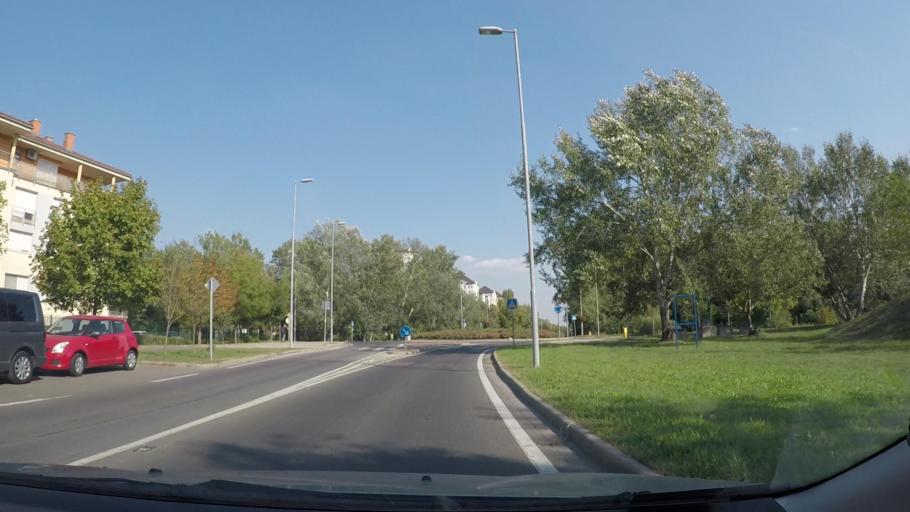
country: HU
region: Budapest
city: Budapest XV. keruelet
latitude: 47.5941
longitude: 19.1118
